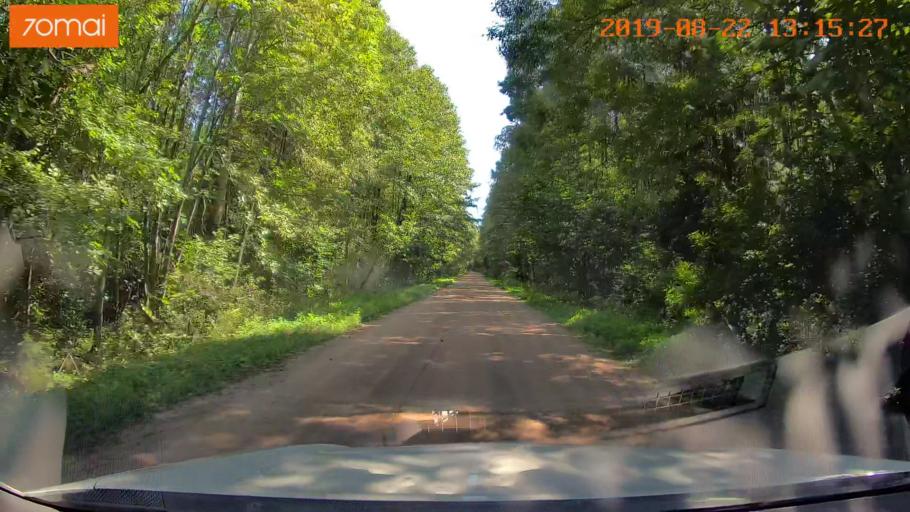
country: BY
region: Minsk
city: Prawdzinski
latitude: 53.2601
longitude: 27.8967
